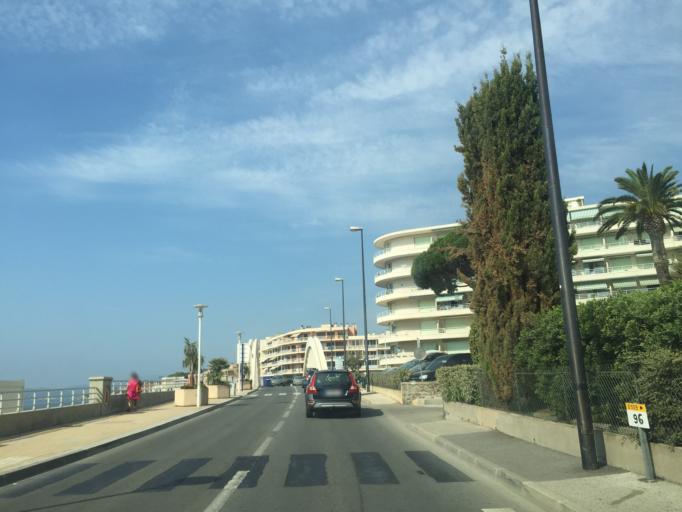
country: FR
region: Provence-Alpes-Cote d'Azur
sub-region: Departement du Var
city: Sainte-Maxime
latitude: 43.3078
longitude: 6.6349
